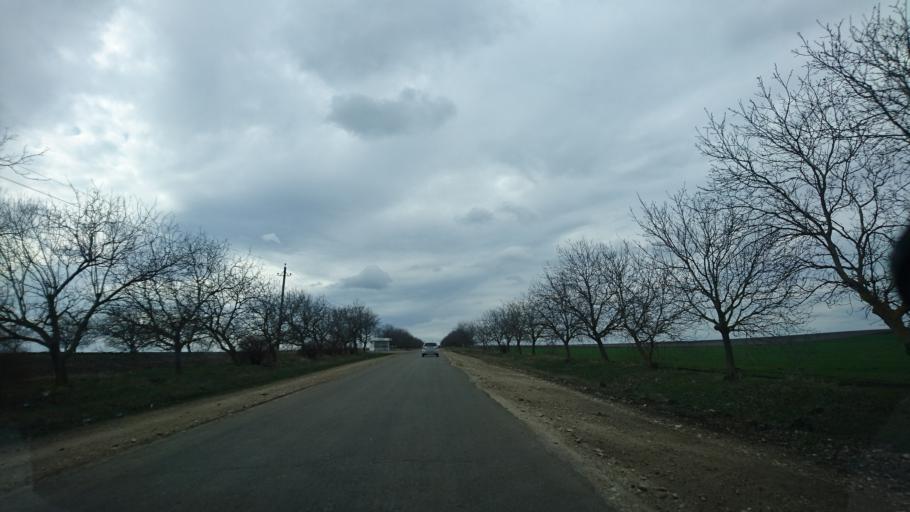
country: MD
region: Gagauzia
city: Comrat
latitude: 46.3151
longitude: 28.5564
